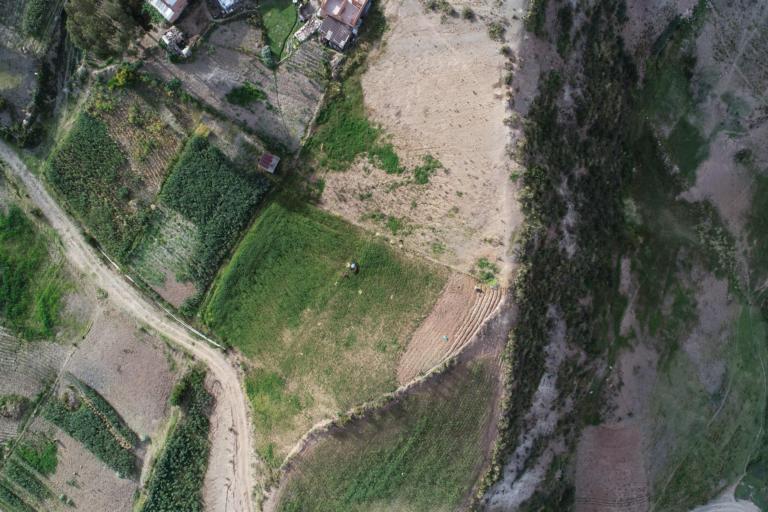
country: BO
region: La Paz
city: La Paz
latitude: -16.5443
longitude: -68.0033
